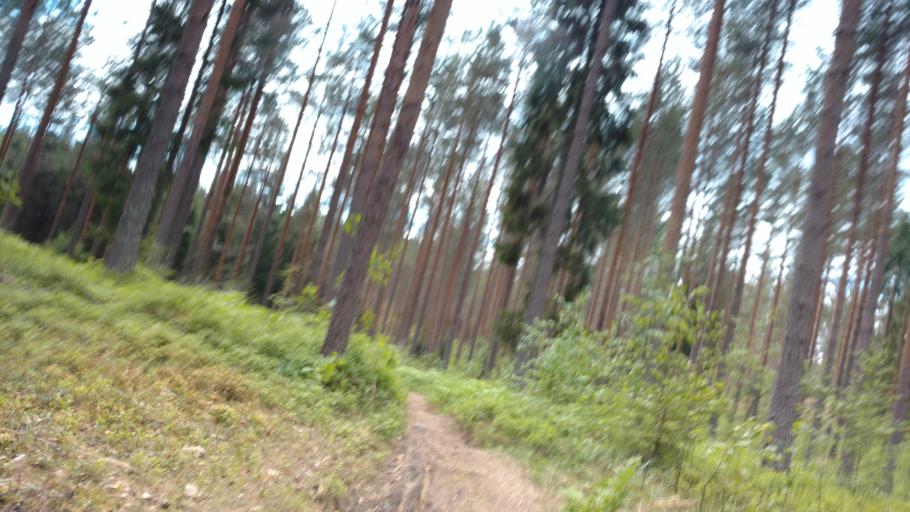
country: FI
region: Uusimaa
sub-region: Raaseporin
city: Pohja
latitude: 60.1184
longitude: 23.5569
